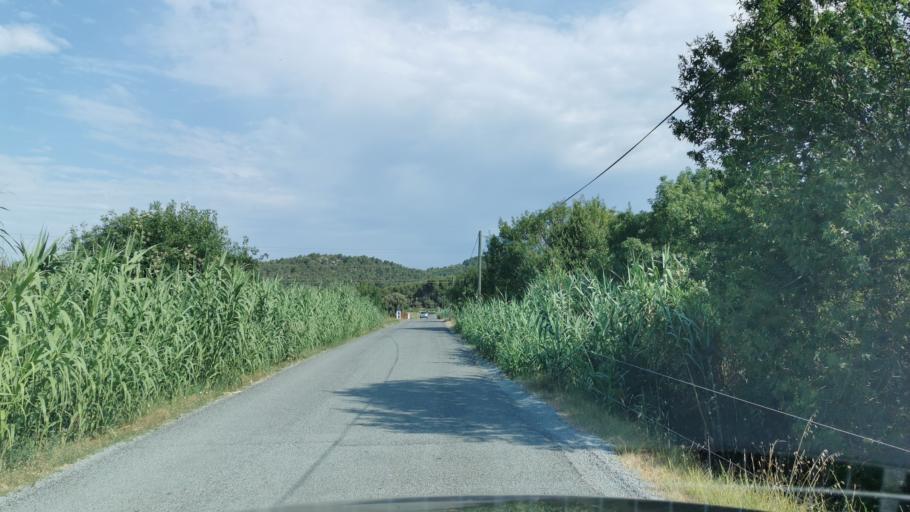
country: FR
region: Languedoc-Roussillon
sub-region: Departement de l'Aude
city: Bize-Minervois
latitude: 43.3394
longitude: 2.8778
